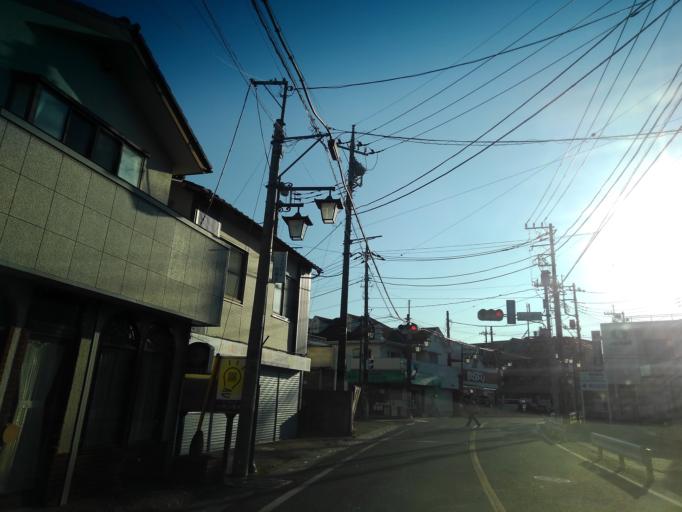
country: JP
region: Saitama
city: Tokorozawa
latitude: 35.7798
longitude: 139.4406
